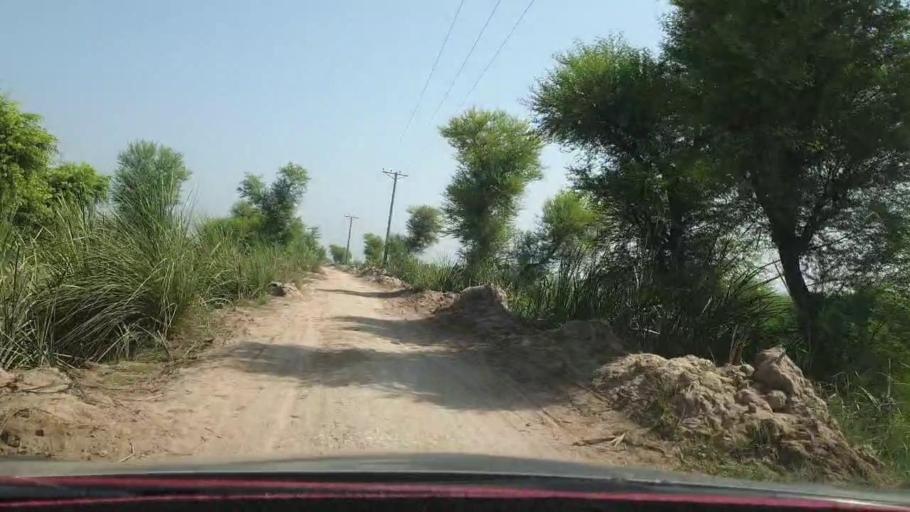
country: PK
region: Sindh
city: Warah
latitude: 27.4860
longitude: 67.8330
